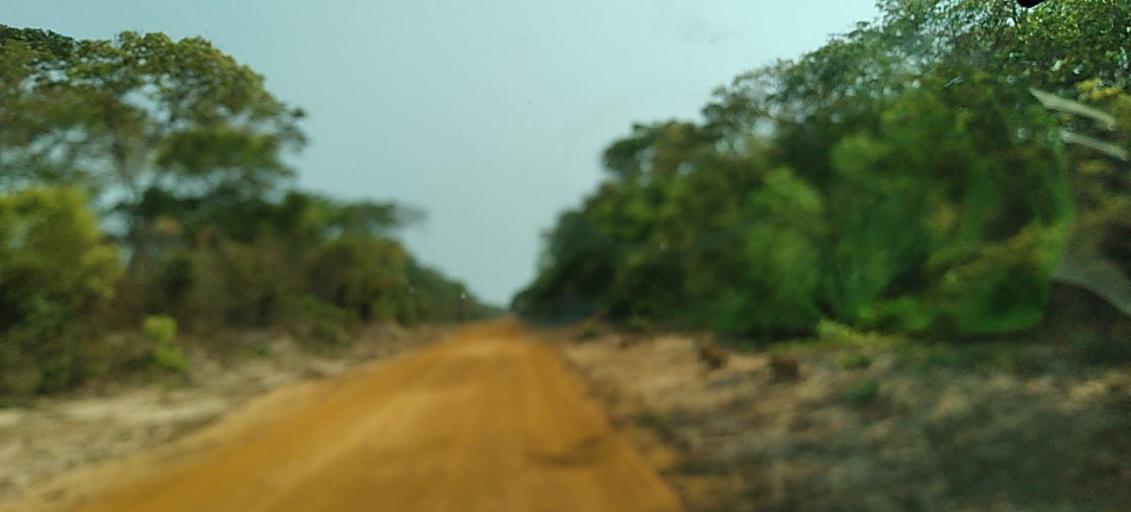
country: ZM
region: North-Western
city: Kabompo
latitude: -13.3415
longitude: 24.0773
